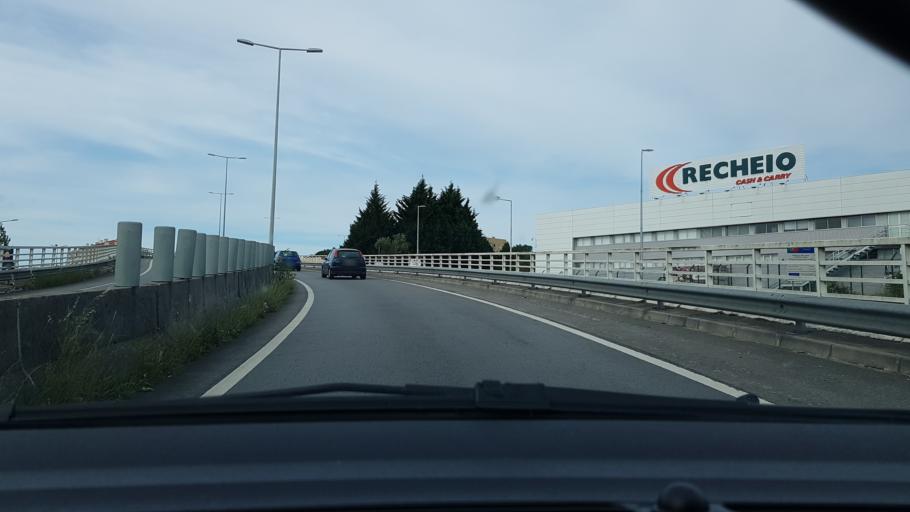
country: PT
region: Porto
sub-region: Gondomar
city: Baguim do Monte
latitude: 41.2041
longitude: -8.5489
